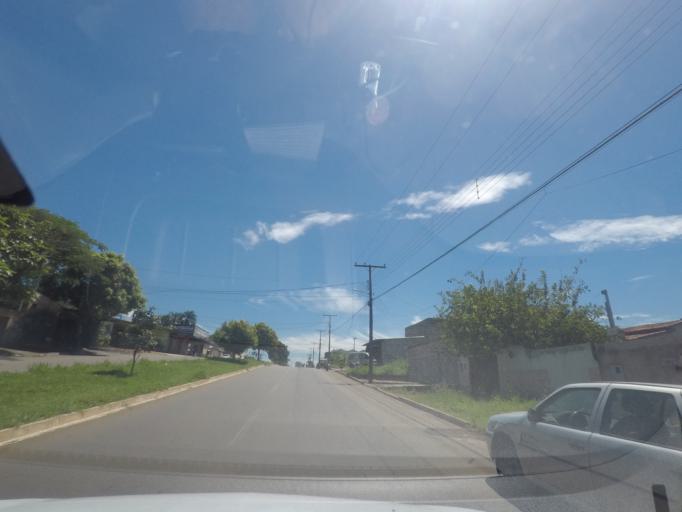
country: BR
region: Goias
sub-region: Aparecida De Goiania
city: Aparecida de Goiania
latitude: -16.7723
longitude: -49.3246
